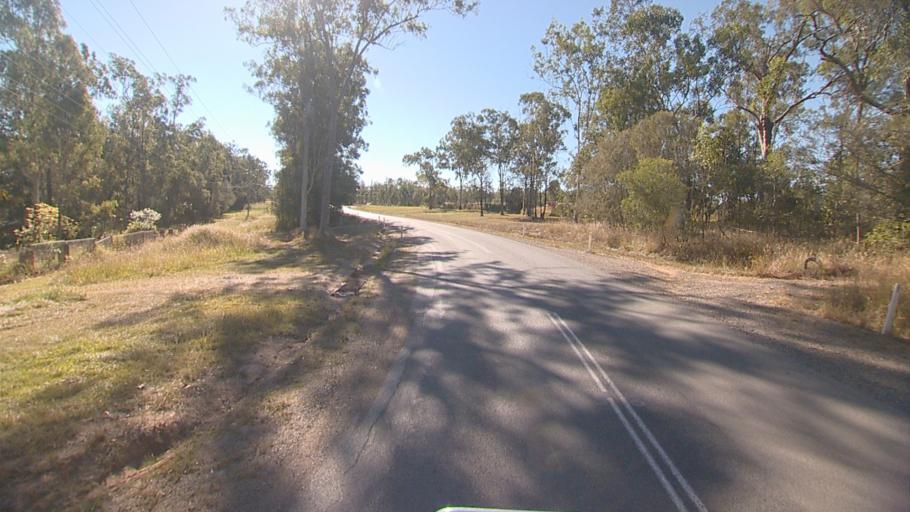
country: AU
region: Queensland
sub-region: Logan
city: North Maclean
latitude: -27.7545
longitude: 152.9960
